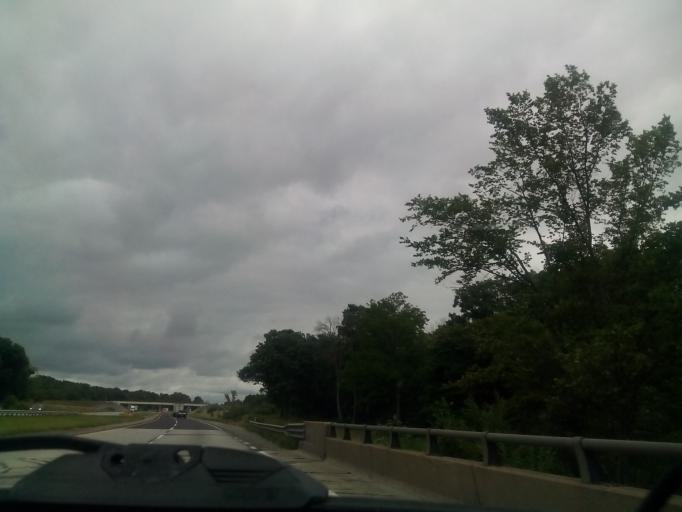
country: US
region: Michigan
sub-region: Branch County
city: Bronson
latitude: 41.7550
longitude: -85.2310
